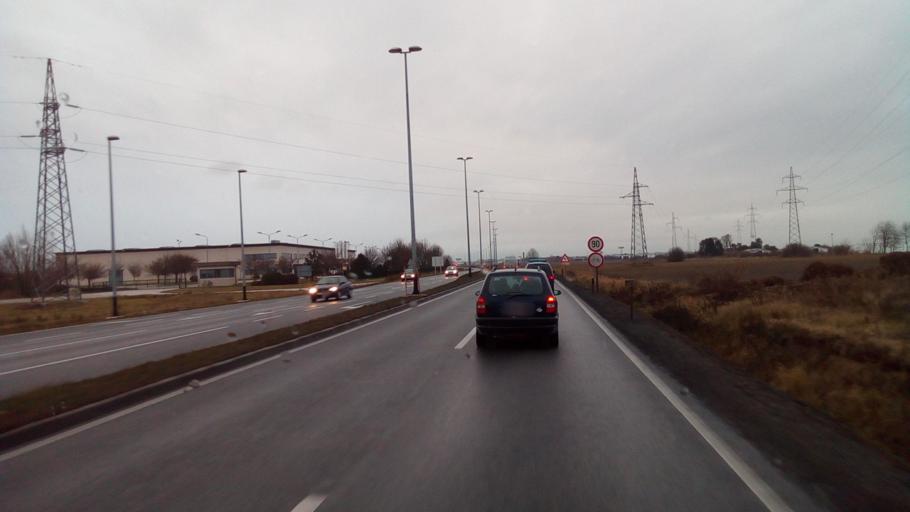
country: HR
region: Varazdinska
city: Varazdin
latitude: 46.2736
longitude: 16.3618
